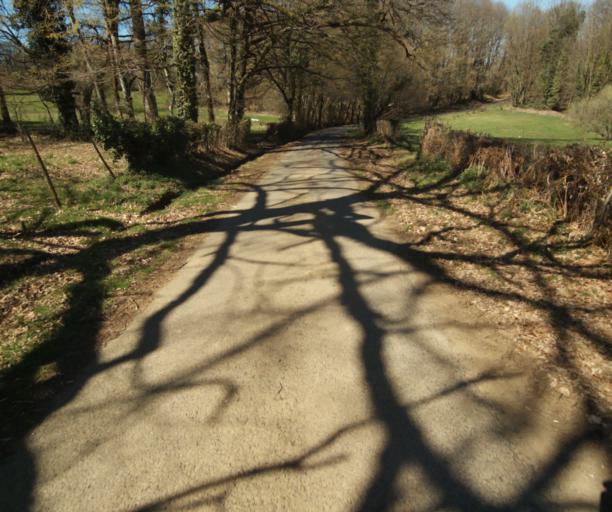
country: FR
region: Limousin
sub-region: Departement de la Correze
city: Saint-Clement
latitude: 45.3864
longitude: 1.6527
